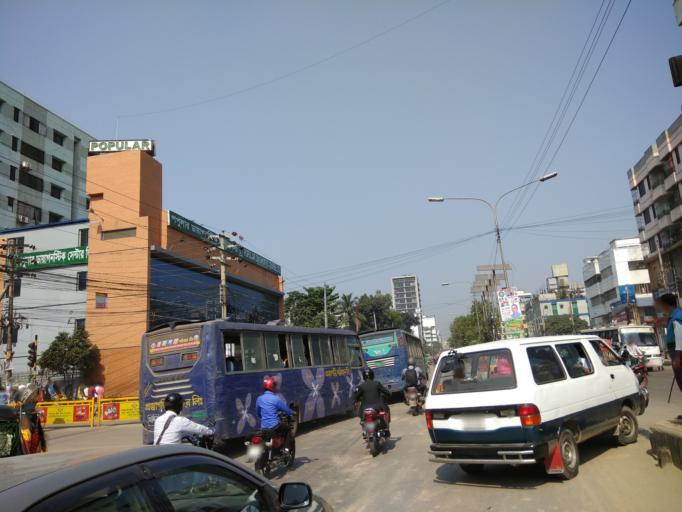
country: BD
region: Dhaka
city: Azimpur
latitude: 23.8103
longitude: 90.3677
